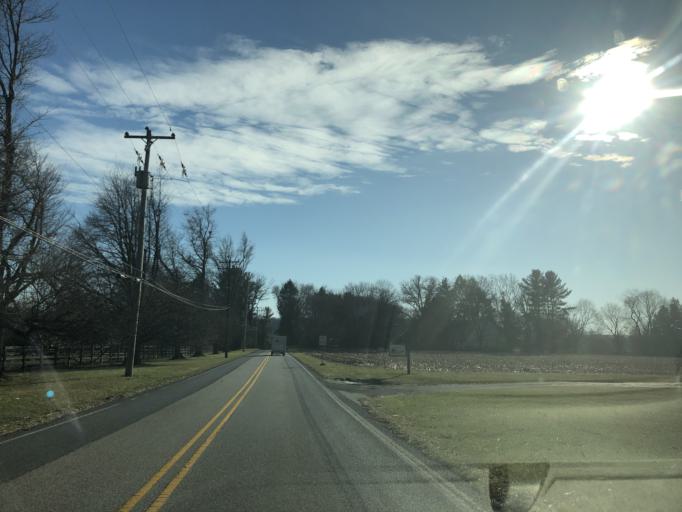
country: US
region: Pennsylvania
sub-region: Chester County
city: Upland
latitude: 39.8594
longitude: -75.7717
